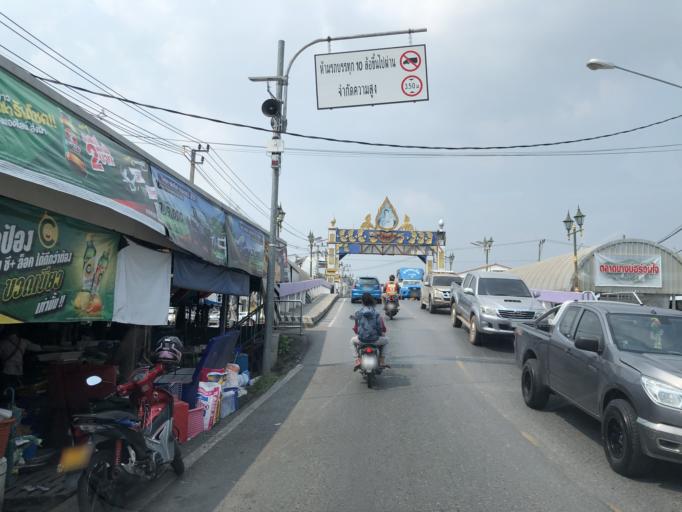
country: TH
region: Samut Prakan
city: Bang Bo
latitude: 13.5732
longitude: 100.8366
